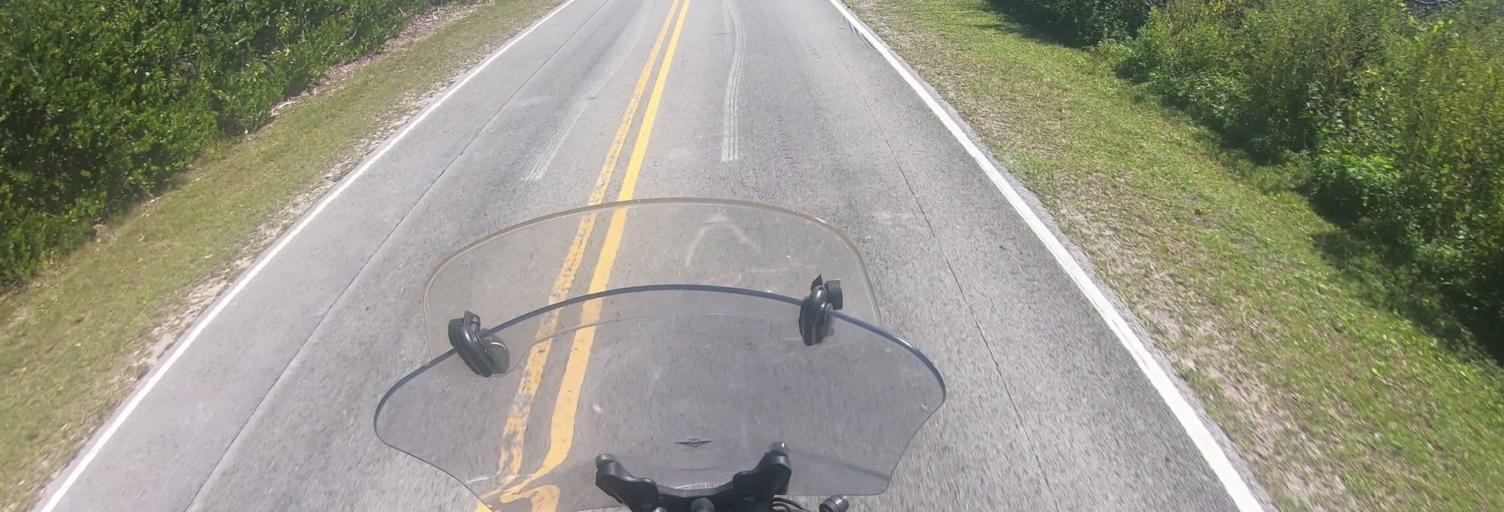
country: US
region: Florida
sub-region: Miami-Dade County
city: Kendall West
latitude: 25.7610
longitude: -80.8607
